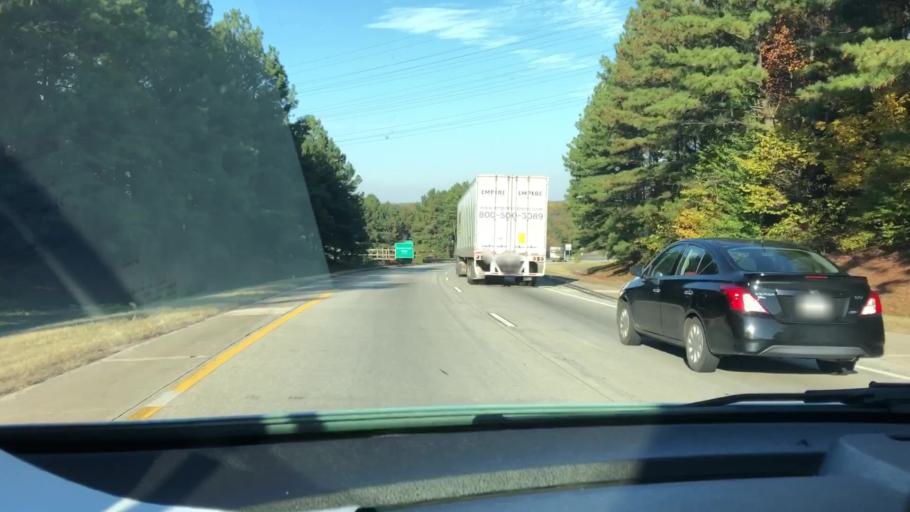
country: US
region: Georgia
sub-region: Clayton County
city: Conley
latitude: 33.6729
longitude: -84.3252
